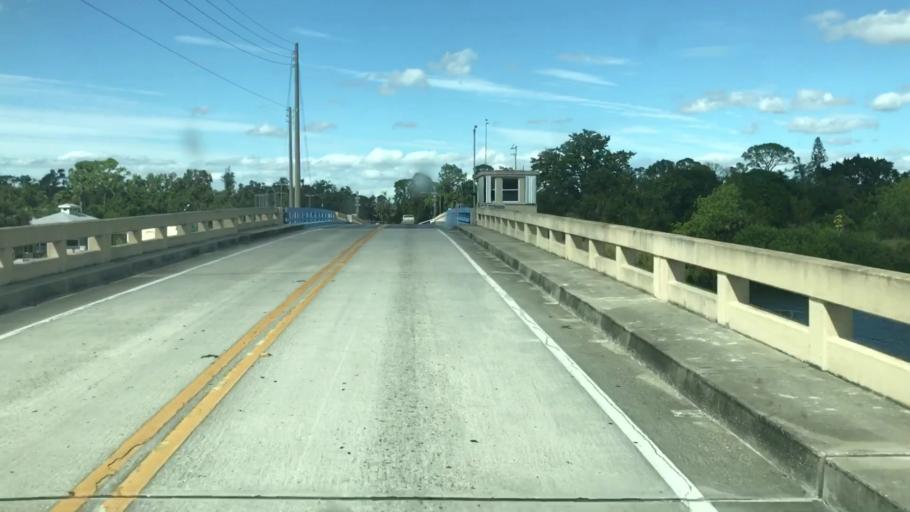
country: US
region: Florida
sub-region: Lee County
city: Alva
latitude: 26.7130
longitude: -81.6100
